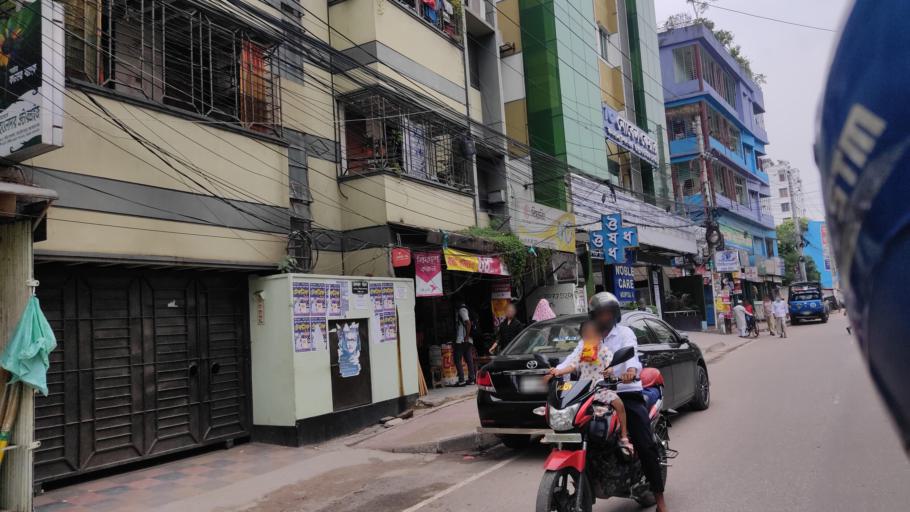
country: BD
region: Dhaka
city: Azimpur
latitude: 23.7826
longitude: 90.3686
